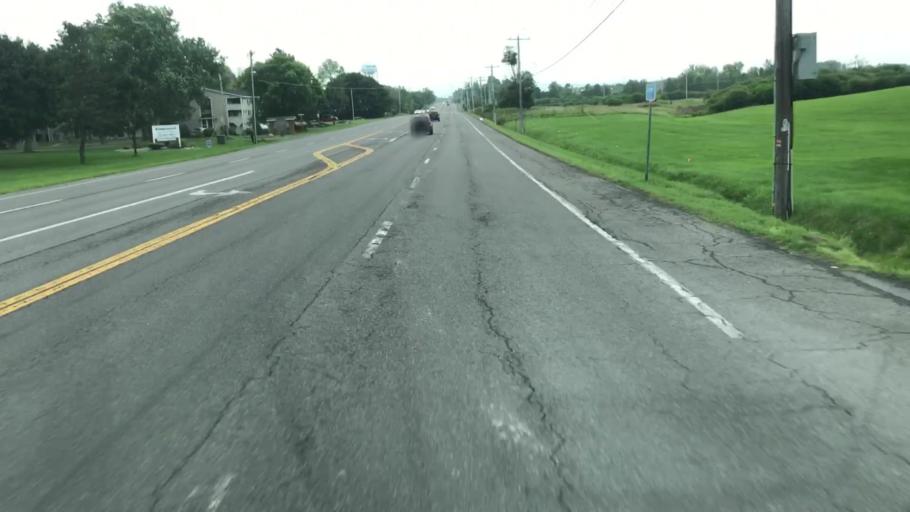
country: US
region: New York
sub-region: Onondaga County
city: Liverpool
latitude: 43.1304
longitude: -76.1867
